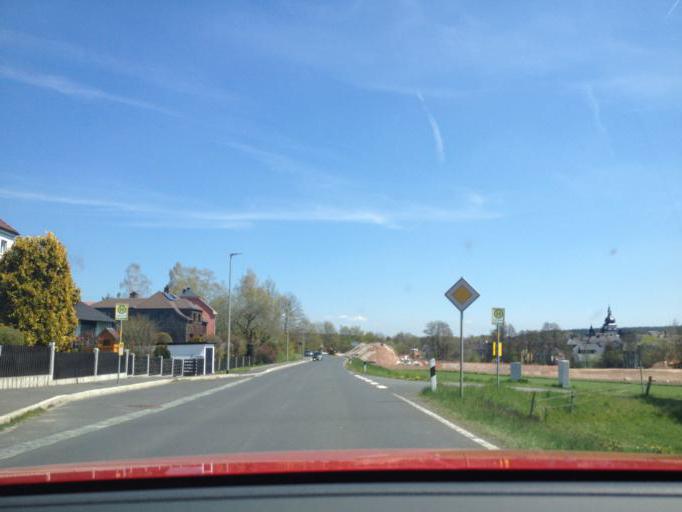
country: DE
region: Bavaria
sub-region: Upper Franconia
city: Marktleuthen
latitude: 50.1298
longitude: 11.9886
